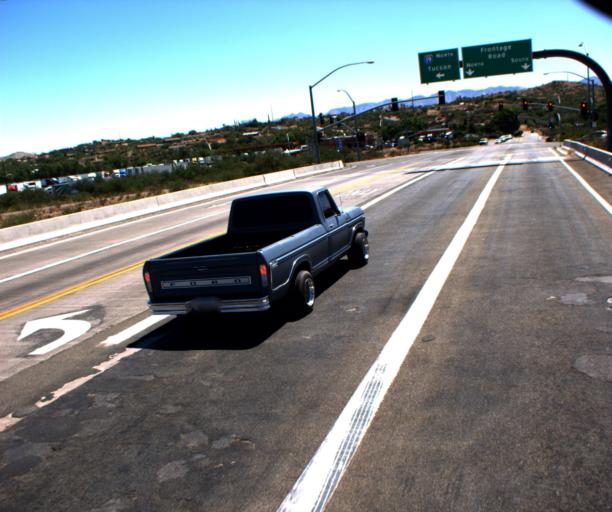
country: US
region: Arizona
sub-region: Santa Cruz County
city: Rio Rico
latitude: 31.4302
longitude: -110.9650
